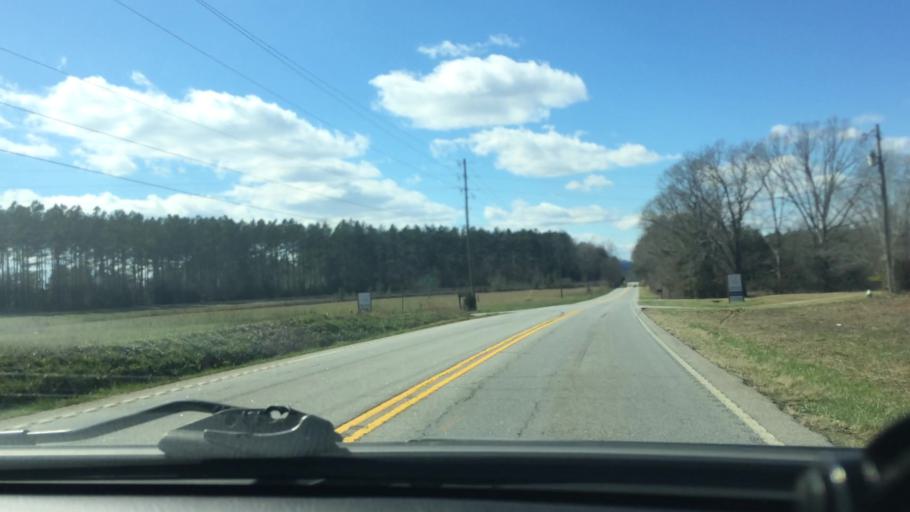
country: US
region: South Carolina
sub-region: Pickens County
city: Easley
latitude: 34.8900
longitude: -82.5719
